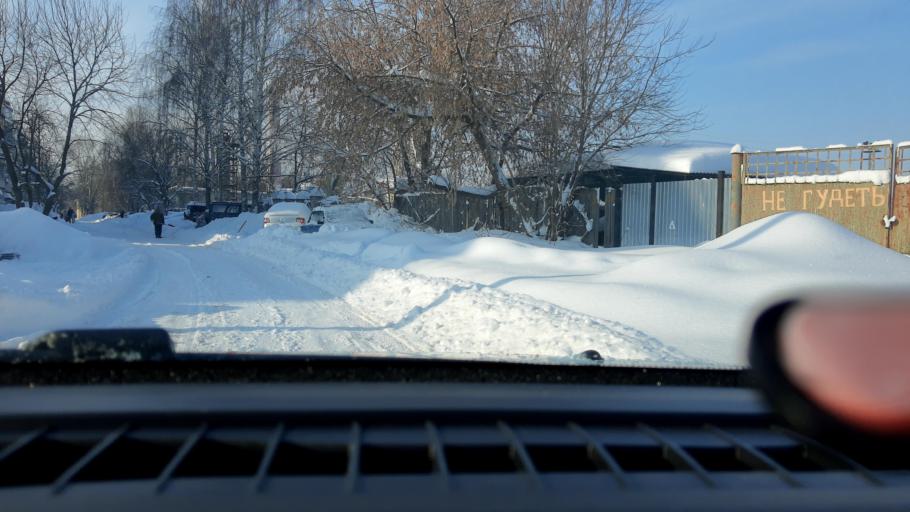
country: RU
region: Nizjnij Novgorod
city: Neklyudovo
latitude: 56.4054
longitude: 43.9965
